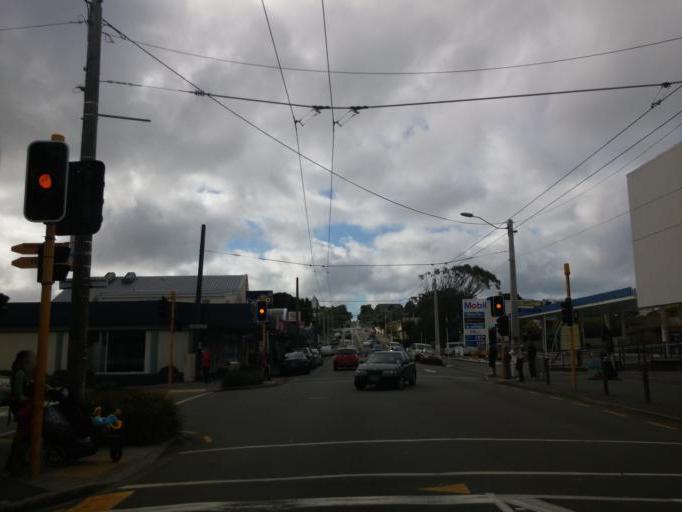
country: NZ
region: Wellington
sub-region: Wellington City
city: Kelburn
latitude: -41.2847
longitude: 174.7373
